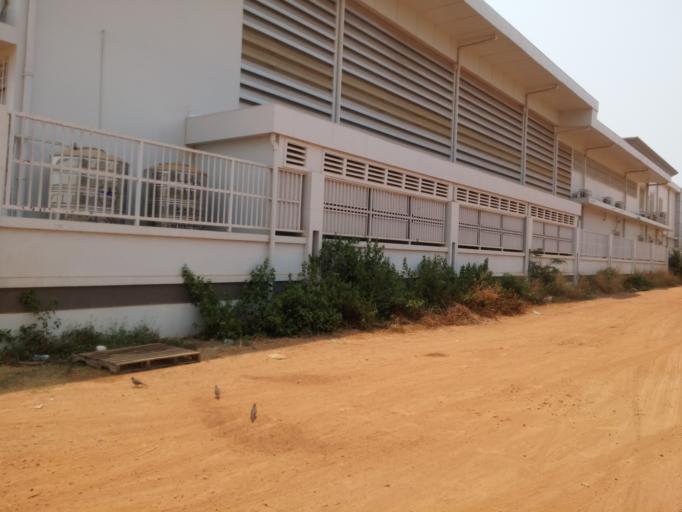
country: KH
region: Siem Reap
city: Siem Reap
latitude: 13.3590
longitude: 103.8908
